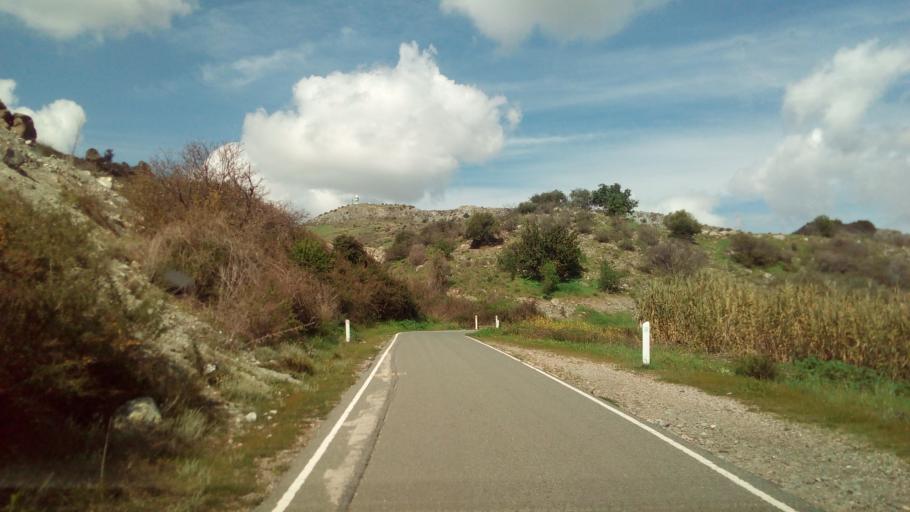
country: CY
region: Pafos
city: Mesogi
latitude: 34.7631
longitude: 32.5536
